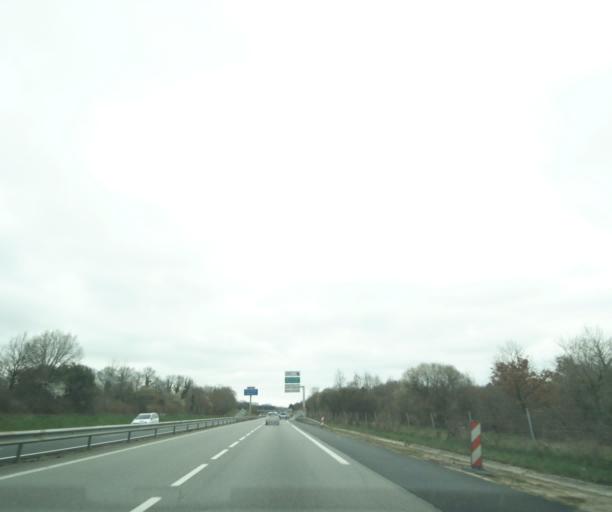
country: FR
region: Limousin
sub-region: Departement de la Haute-Vienne
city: Rilhac-Rancon
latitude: 45.8983
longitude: 1.2921
